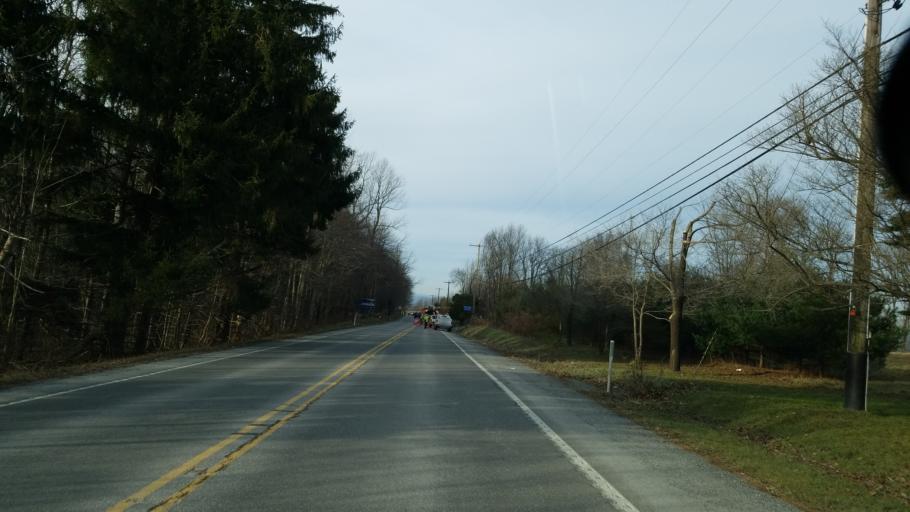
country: US
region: Pennsylvania
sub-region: Clearfield County
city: Sandy
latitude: 41.0462
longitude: -78.7024
